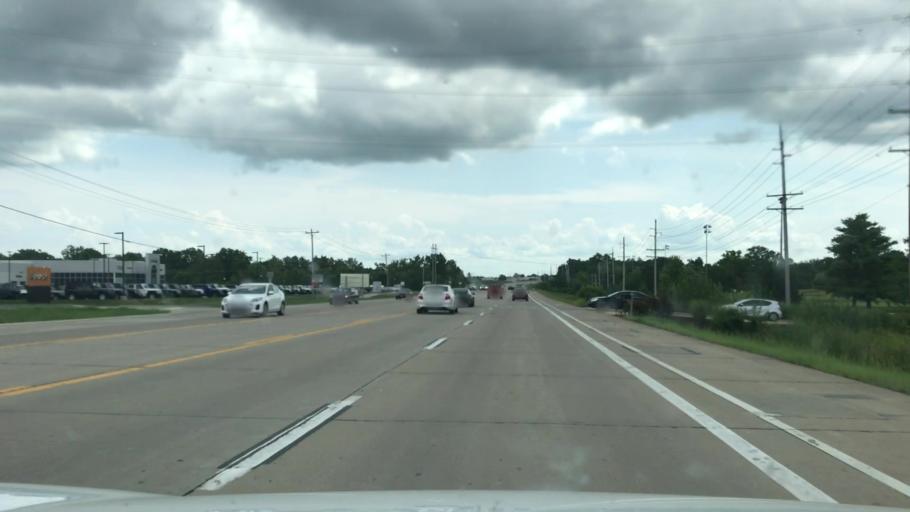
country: US
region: Missouri
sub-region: Saint Charles County
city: Weldon Spring
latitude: 38.7442
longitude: -90.6977
